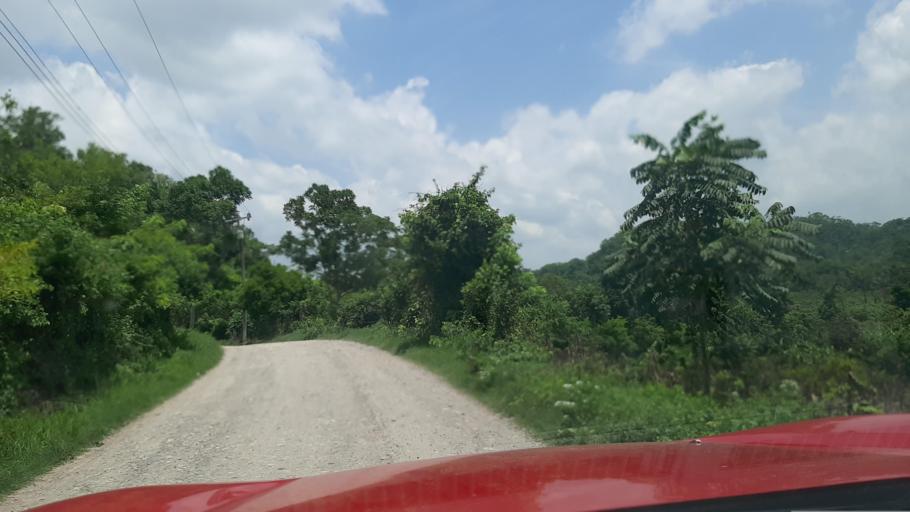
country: MX
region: Veracruz
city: Papantla de Olarte
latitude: 20.4360
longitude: -97.2704
